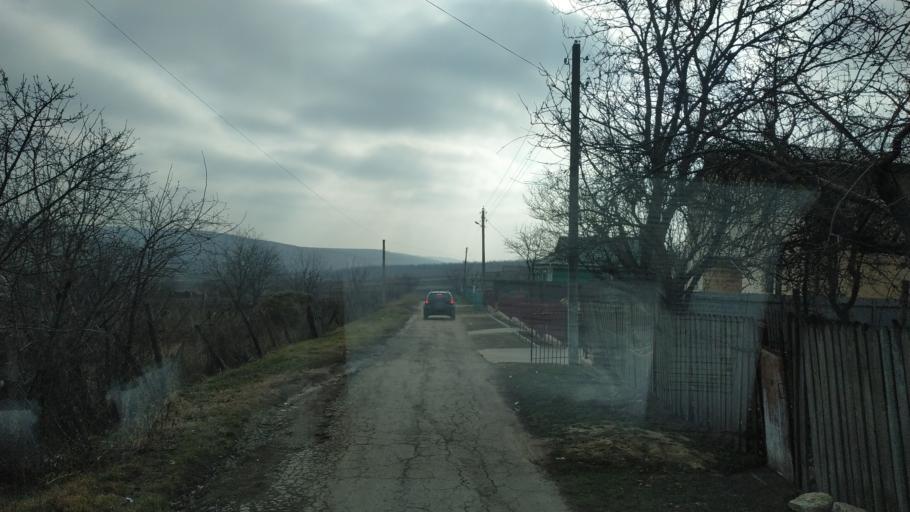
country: MD
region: Hincesti
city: Dancu
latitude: 46.8795
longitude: 28.3181
